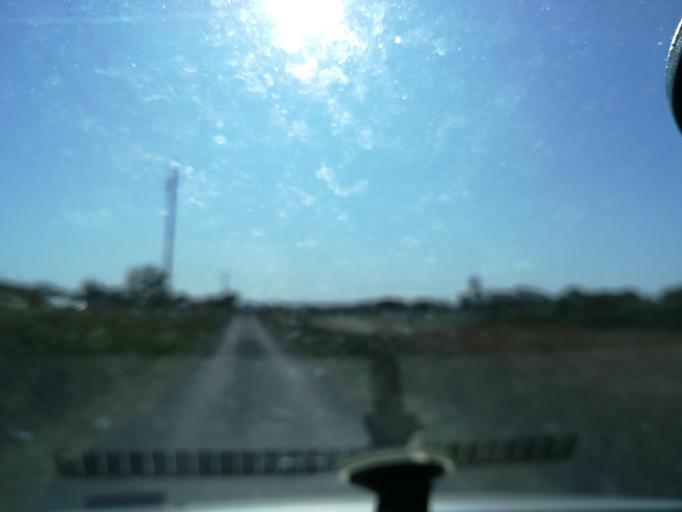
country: FR
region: Languedoc-Roussillon
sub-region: Departement de l'Herault
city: Portiragnes
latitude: 43.2907
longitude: 3.3766
